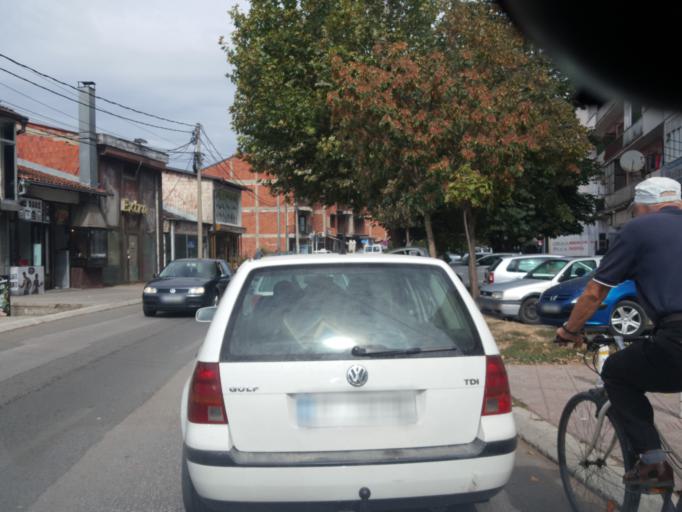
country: XK
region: Gjakova
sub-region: Komuna e Gjakoves
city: Gjakove
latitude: 42.3847
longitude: 20.4281
